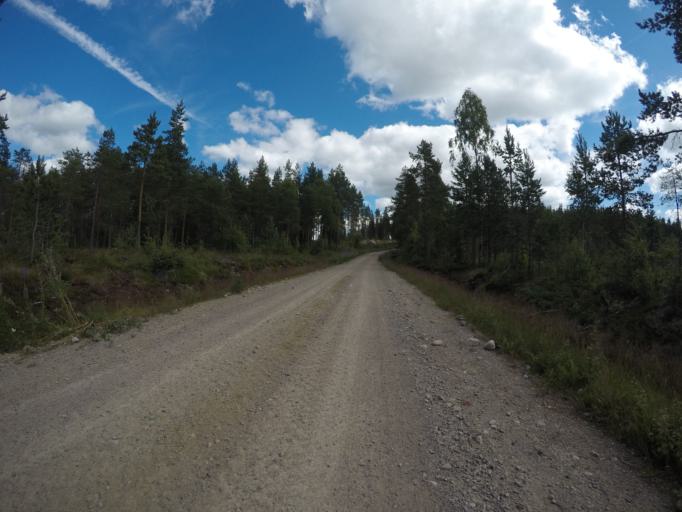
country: SE
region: OErebro
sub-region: Hallefors Kommun
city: Haellefors
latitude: 60.0704
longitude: 14.4739
